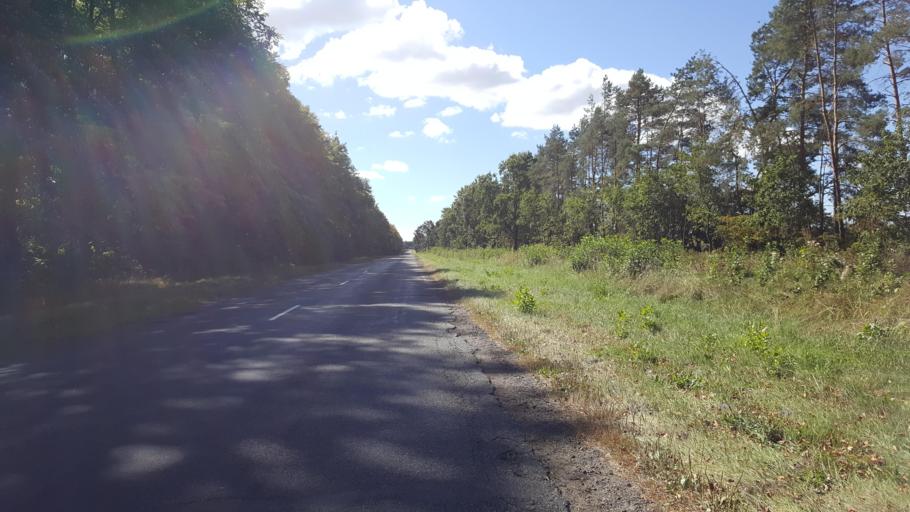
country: BY
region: Brest
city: Vysokaye
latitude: 52.3327
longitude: 23.3300
